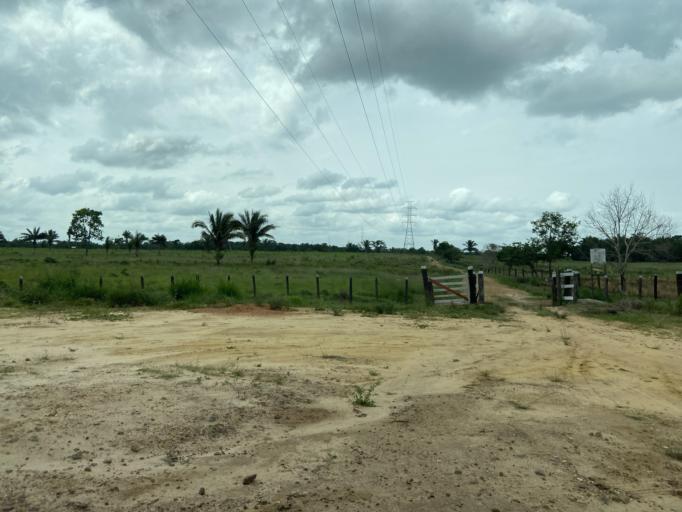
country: BR
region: Para
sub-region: Maraba
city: Maraba
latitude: -5.2659
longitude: -49.0050
